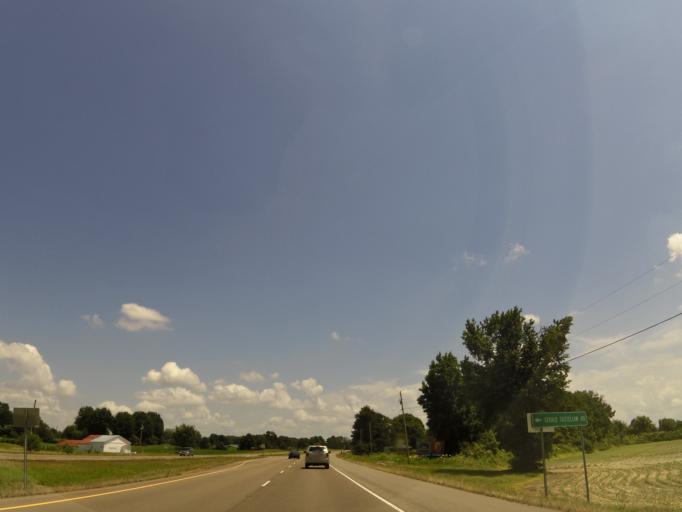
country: US
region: Tennessee
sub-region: Crockett County
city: Alamo
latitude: 35.8531
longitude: -89.1983
